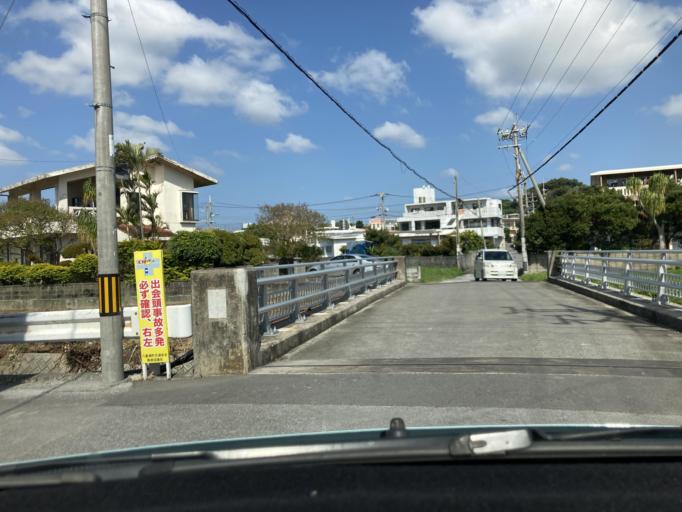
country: JP
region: Okinawa
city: Itoman
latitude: 26.1222
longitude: 127.7478
